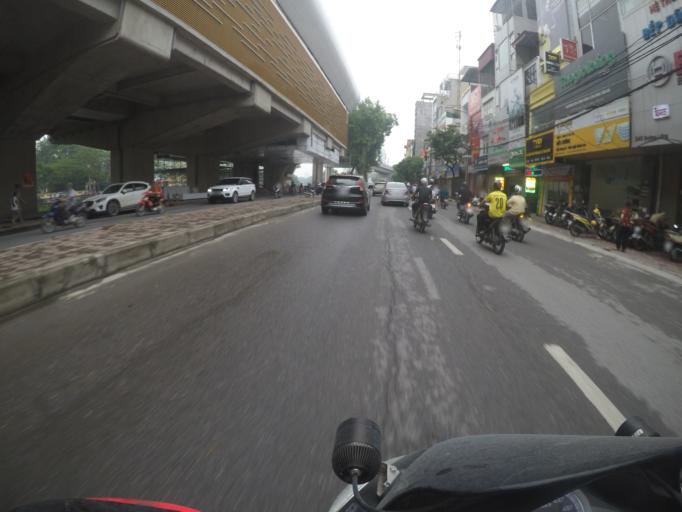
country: VN
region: Ha Noi
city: Dong Da
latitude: 21.0066
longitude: 105.8162
